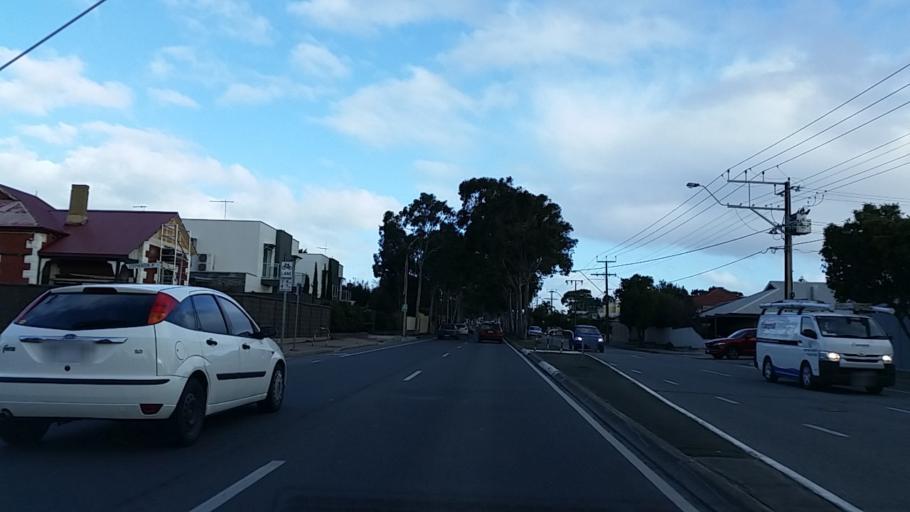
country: AU
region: South Australia
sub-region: Adelaide
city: Brighton
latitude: -35.0264
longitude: 138.5237
